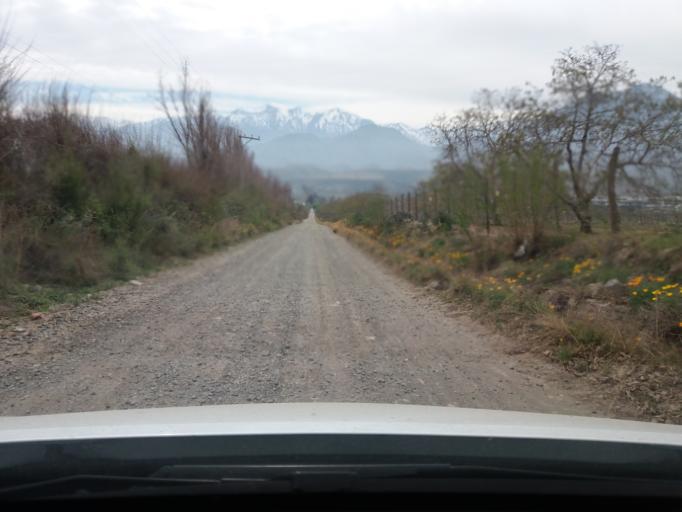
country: CL
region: Valparaiso
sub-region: Provincia de Los Andes
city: Los Andes
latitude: -32.8447
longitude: -70.5531
